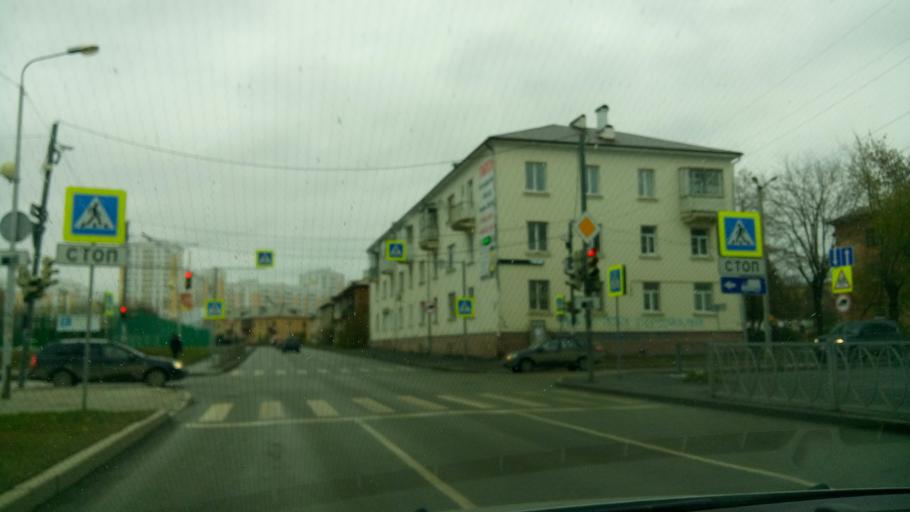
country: RU
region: Sverdlovsk
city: Verkhnyaya Pyshma
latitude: 56.9689
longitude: 60.5799
